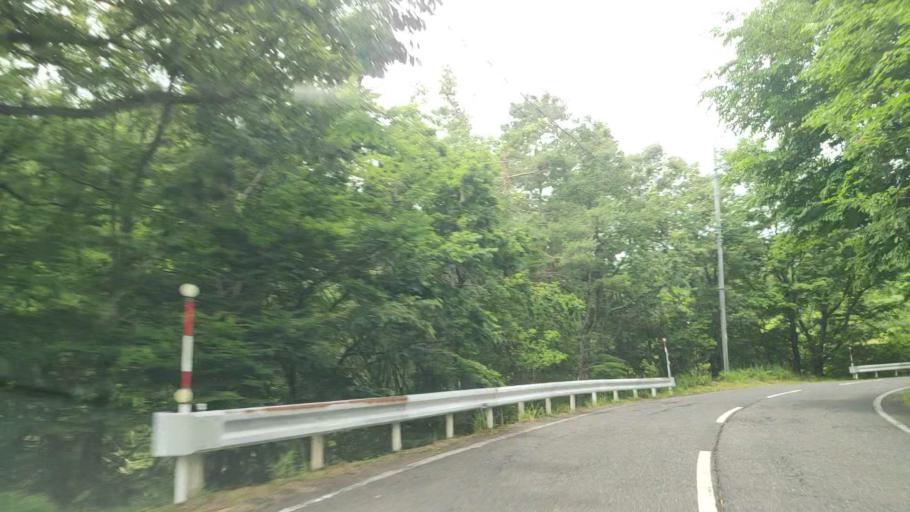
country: JP
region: Hyogo
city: Toyooka
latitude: 35.5188
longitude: 134.6932
